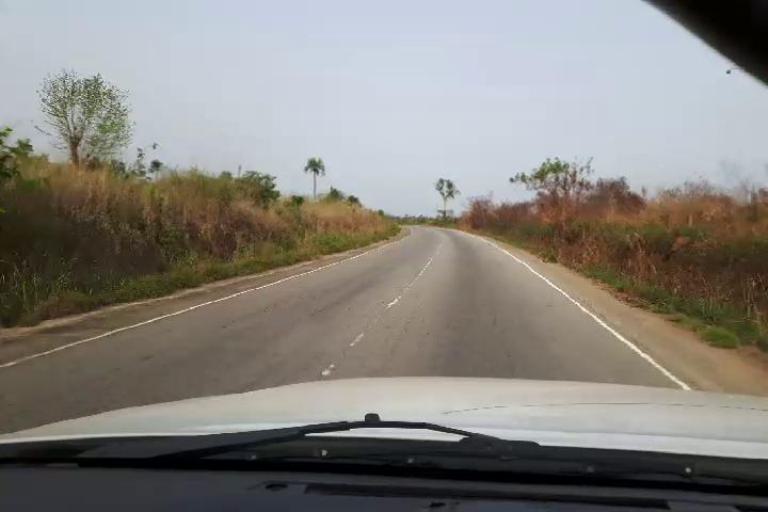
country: SL
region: Southern Province
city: Baoma
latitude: 7.9266
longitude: -11.5858
